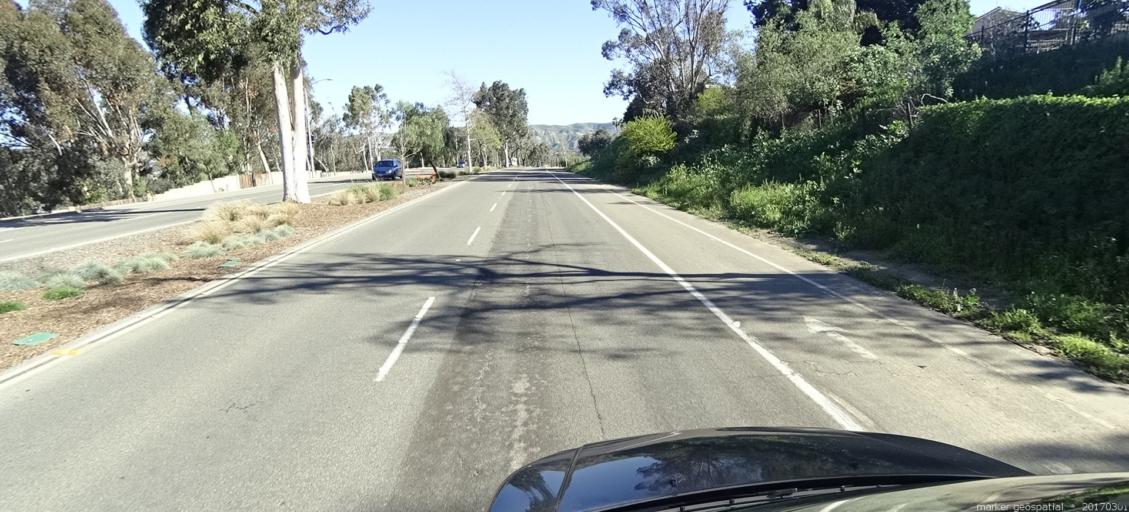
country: US
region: California
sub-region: Orange County
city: Yorba Linda
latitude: 33.8632
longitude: -117.7642
